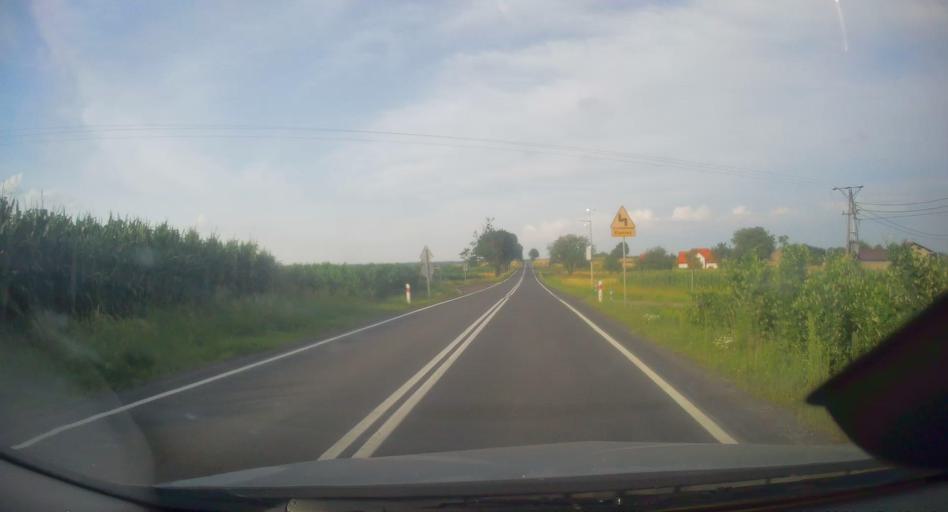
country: PL
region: Lesser Poland Voivodeship
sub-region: Powiat bochenski
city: Dziewin
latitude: 50.1509
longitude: 20.5240
